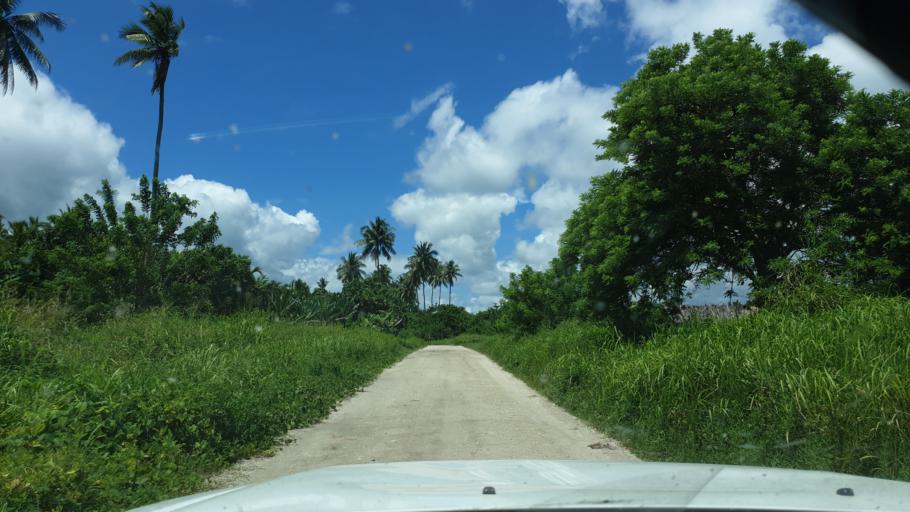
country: PG
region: East Sepik
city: Angoram
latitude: -4.2012
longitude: 144.8875
